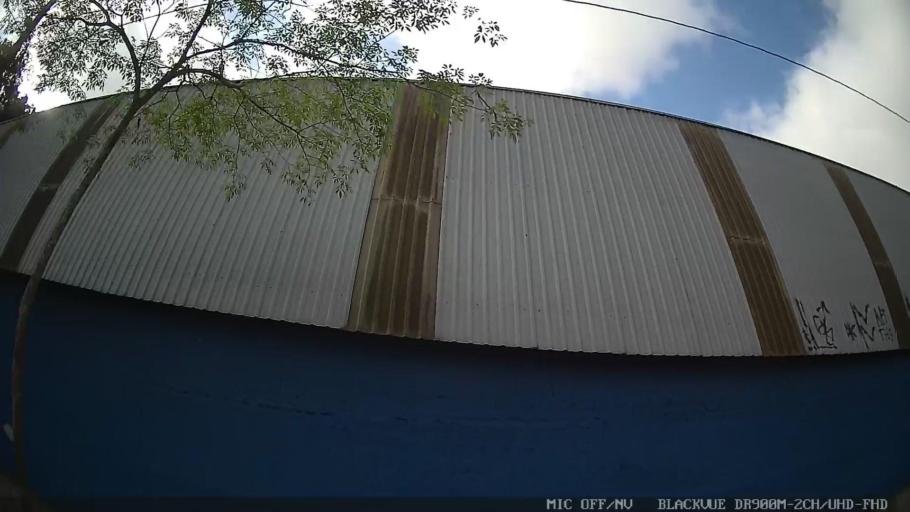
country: BR
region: Sao Paulo
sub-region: Sao Caetano Do Sul
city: Sao Caetano do Sul
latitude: -23.5708
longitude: -46.5307
